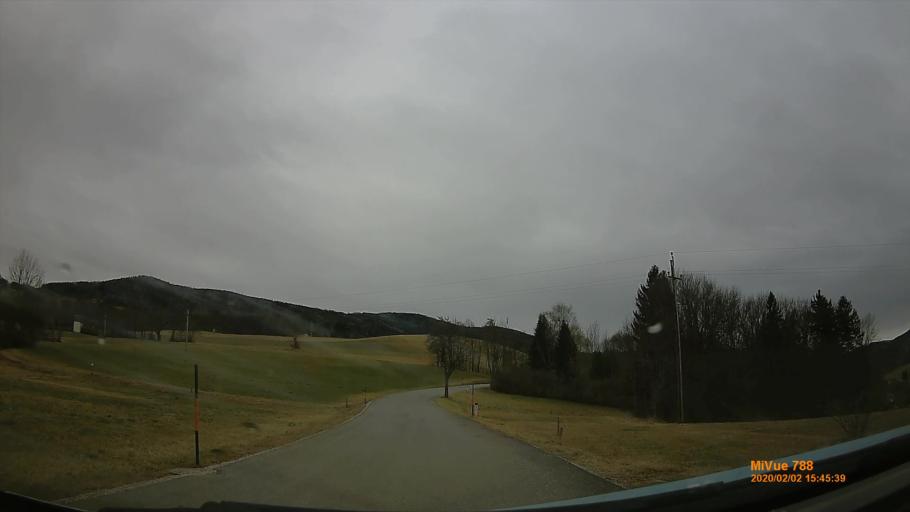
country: AT
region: Lower Austria
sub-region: Politischer Bezirk Neunkirchen
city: Reichenau an der Rax
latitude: 47.6966
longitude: 15.8211
